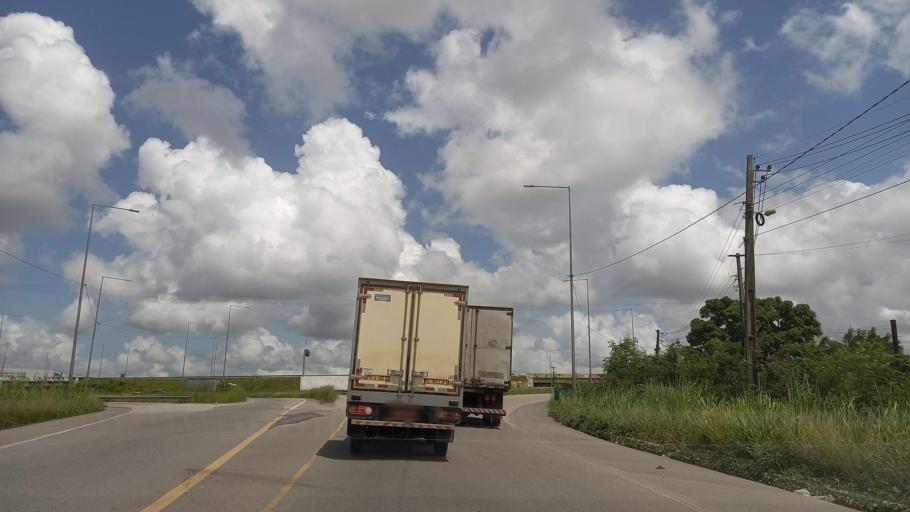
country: BR
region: Pernambuco
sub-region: Cabo De Santo Agostinho
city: Cabo
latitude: -8.2500
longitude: -35.0048
